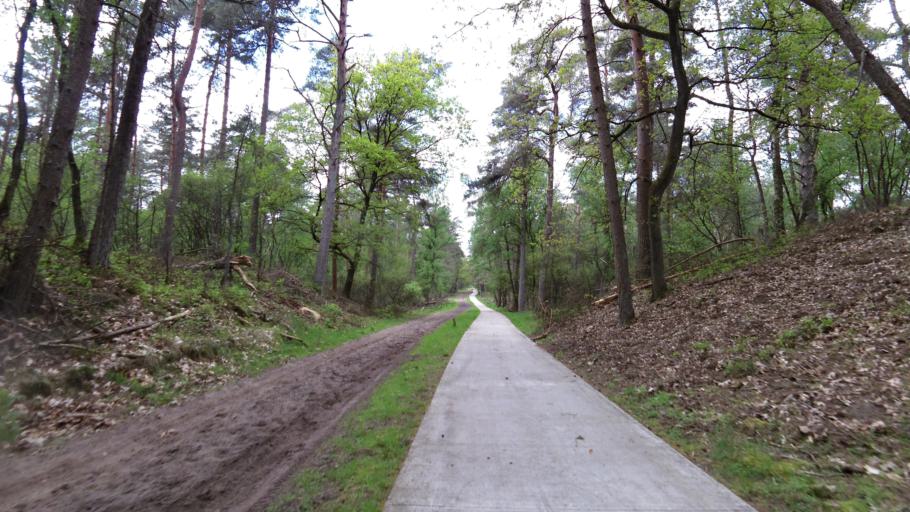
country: NL
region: Gelderland
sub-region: Gemeente Brummen
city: Eerbeek
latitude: 52.0701
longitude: 6.0624
